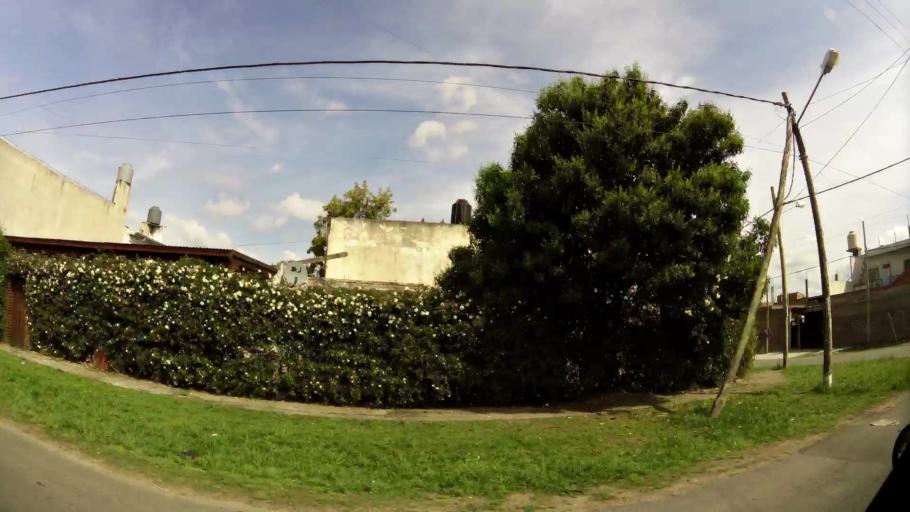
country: AR
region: Buenos Aires
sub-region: Partido de Quilmes
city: Quilmes
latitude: -34.7631
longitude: -58.2383
